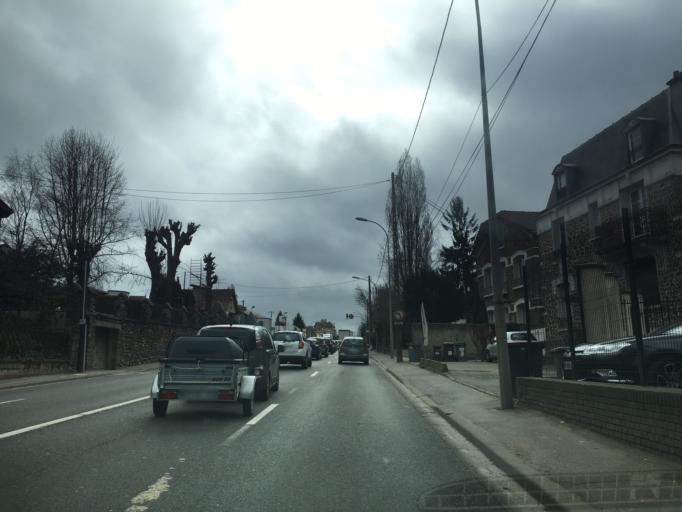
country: FR
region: Ile-de-France
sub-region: Departement du Val-de-Marne
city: Boissy-Saint-Leger
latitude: 48.7506
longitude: 2.5075
